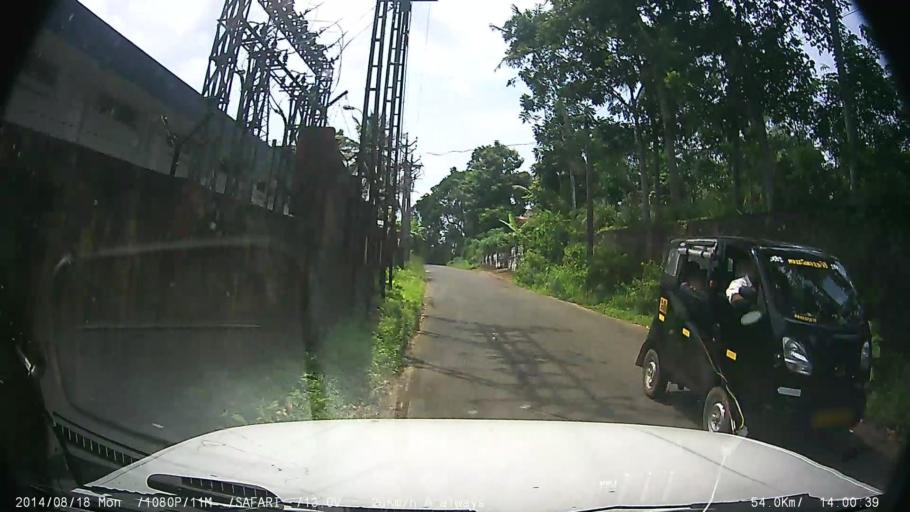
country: IN
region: Kerala
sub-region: Kottayam
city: Palackattumala
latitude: 9.7651
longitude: 76.5652
